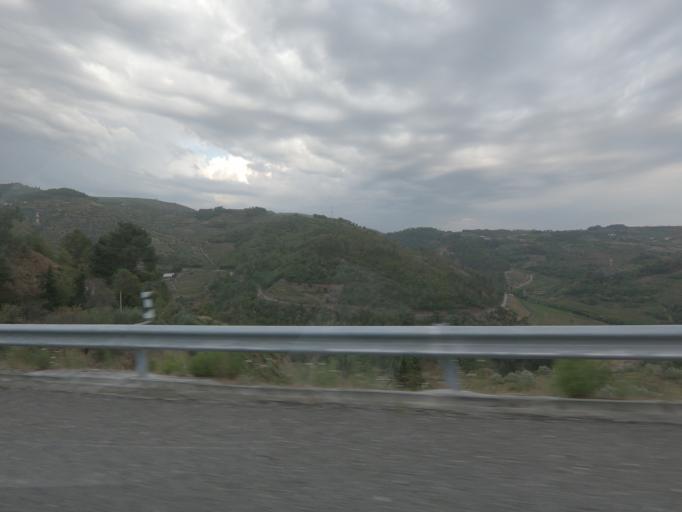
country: PT
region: Viseu
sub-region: Lamego
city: Lamego
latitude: 41.1002
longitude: -7.7791
